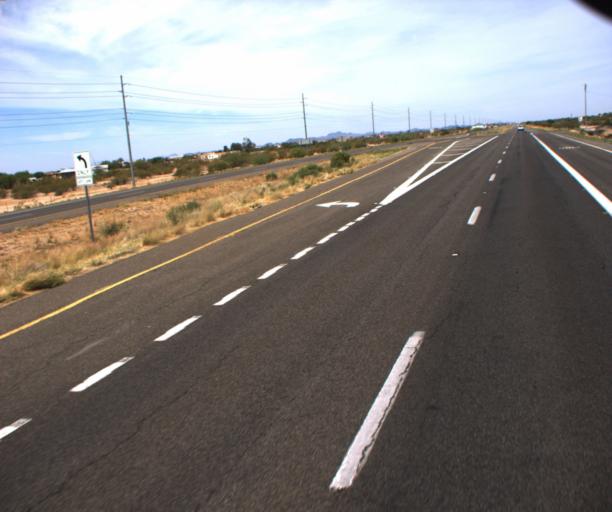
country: US
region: Arizona
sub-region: Maricopa County
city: Sun City West
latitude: 33.7551
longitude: -112.4992
